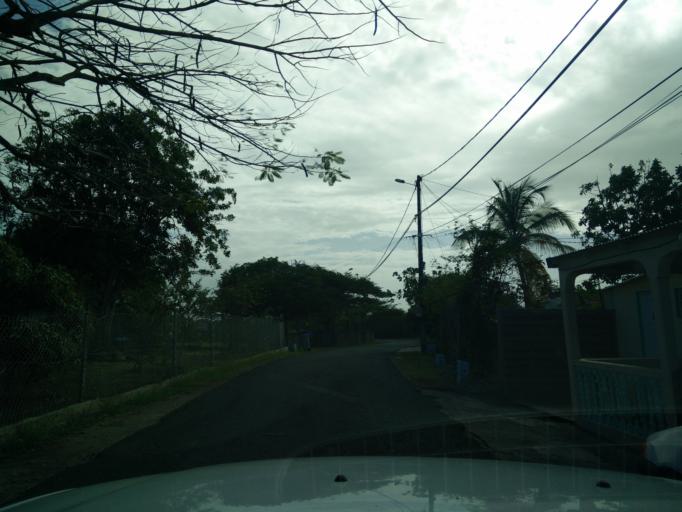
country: GP
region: Guadeloupe
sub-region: Guadeloupe
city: Sainte-Anne
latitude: 16.2272
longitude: -61.3862
